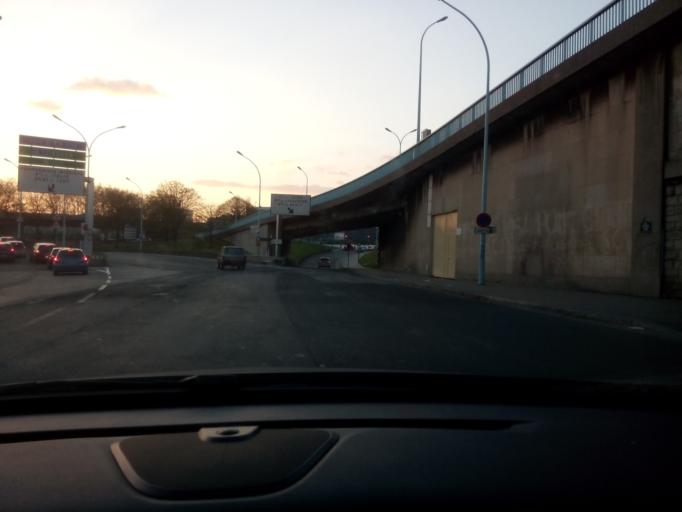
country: FR
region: Ile-de-France
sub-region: Departement du Val-de-Marne
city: Ivry-sur-Seine
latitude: 48.8281
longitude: 2.3921
